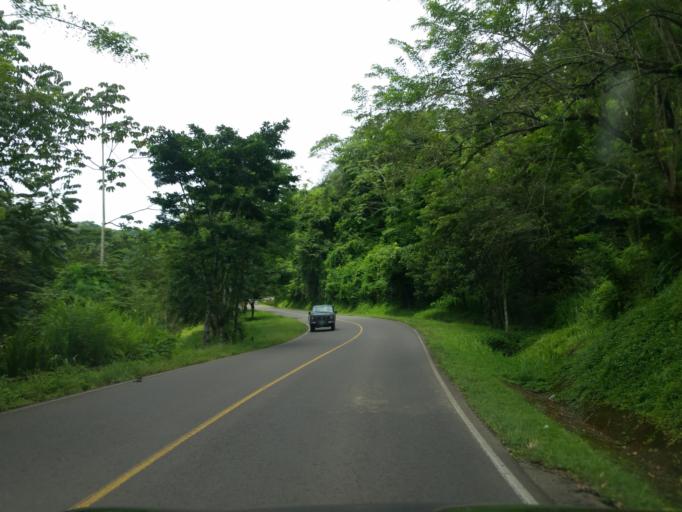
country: NI
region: Matagalpa
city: San Ramon
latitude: 13.0239
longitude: -85.7843
